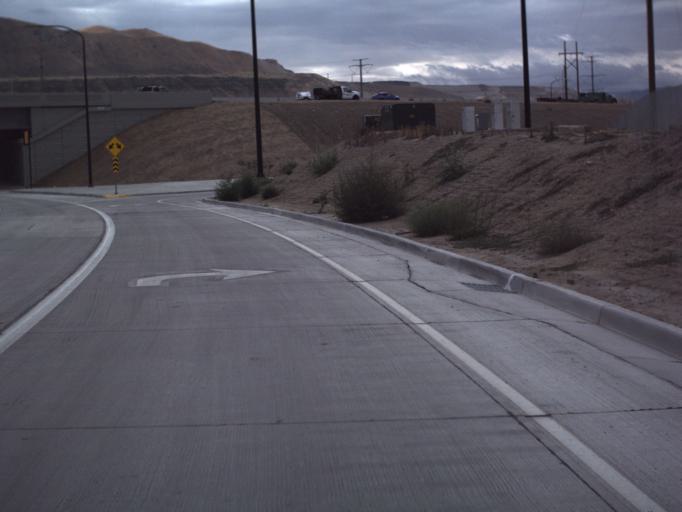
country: US
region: Utah
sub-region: Salt Lake County
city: Bluffdale
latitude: 40.5018
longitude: -111.9083
